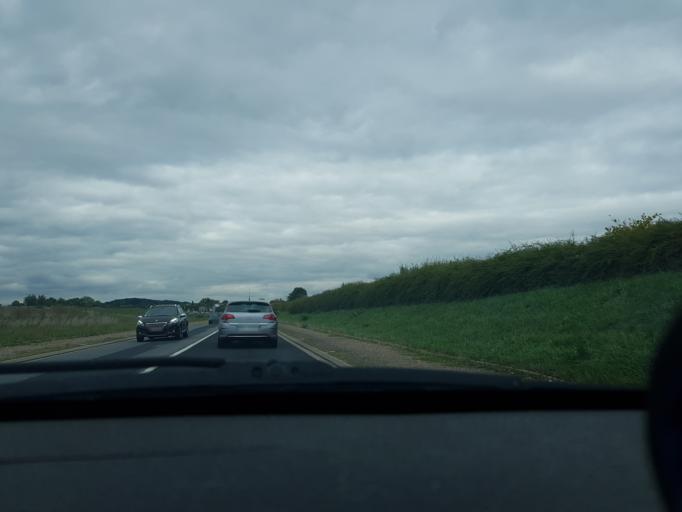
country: FR
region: Lorraine
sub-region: Departement de Meurthe-et-Moselle
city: Tomblaine
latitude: 48.6847
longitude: 6.2254
